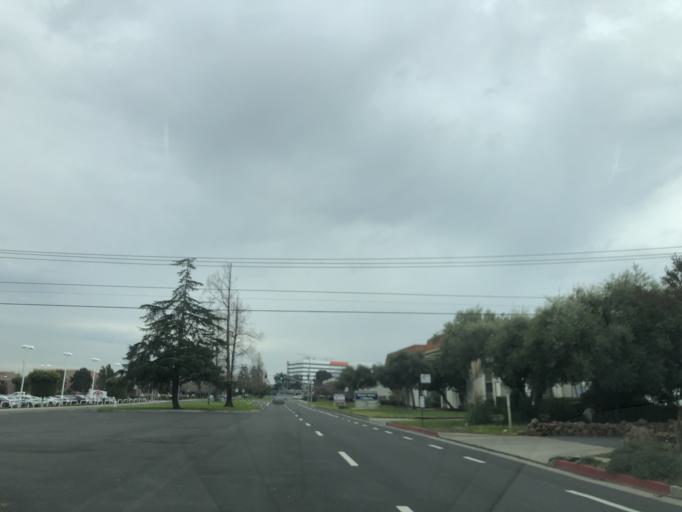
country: US
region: California
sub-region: Alameda County
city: Alameda
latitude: 37.7402
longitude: -122.2017
